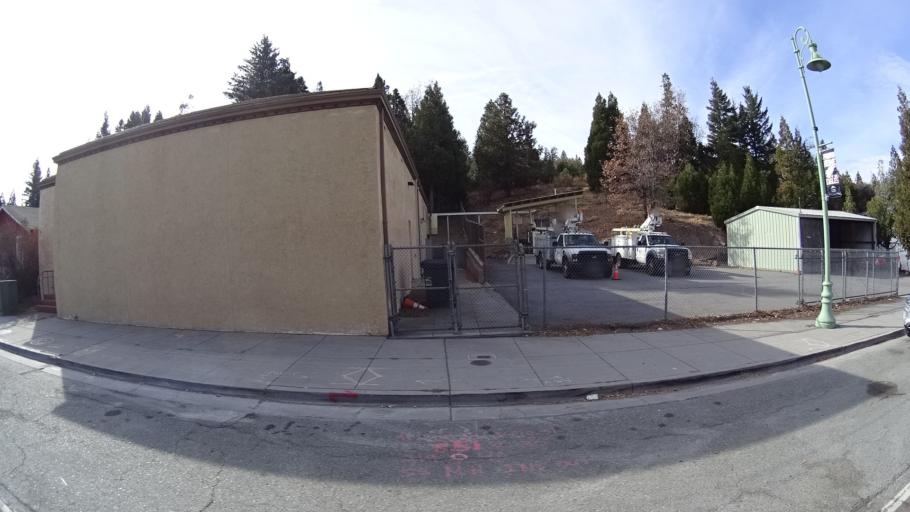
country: US
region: California
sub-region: Siskiyou County
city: Weed
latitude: 41.4207
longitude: -122.3841
